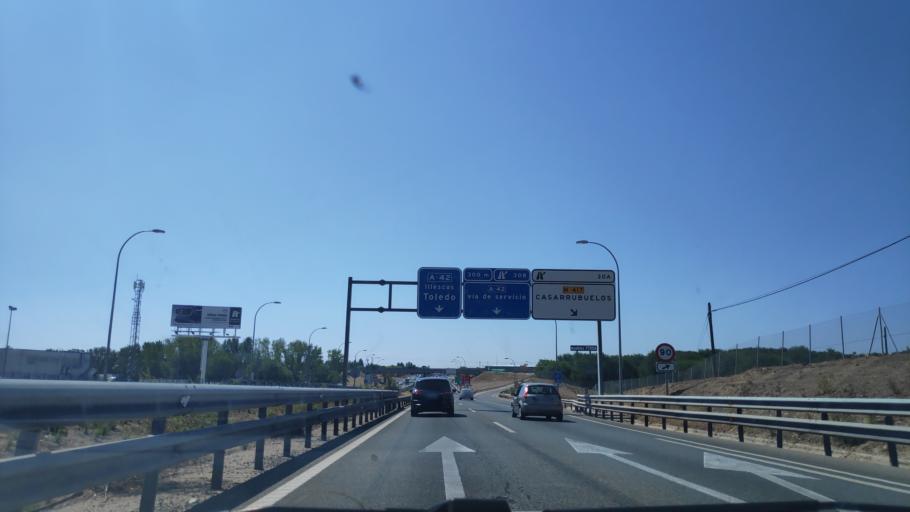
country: ES
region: Madrid
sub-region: Provincia de Madrid
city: Casarrubuelos
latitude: 40.1724
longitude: -3.8129
